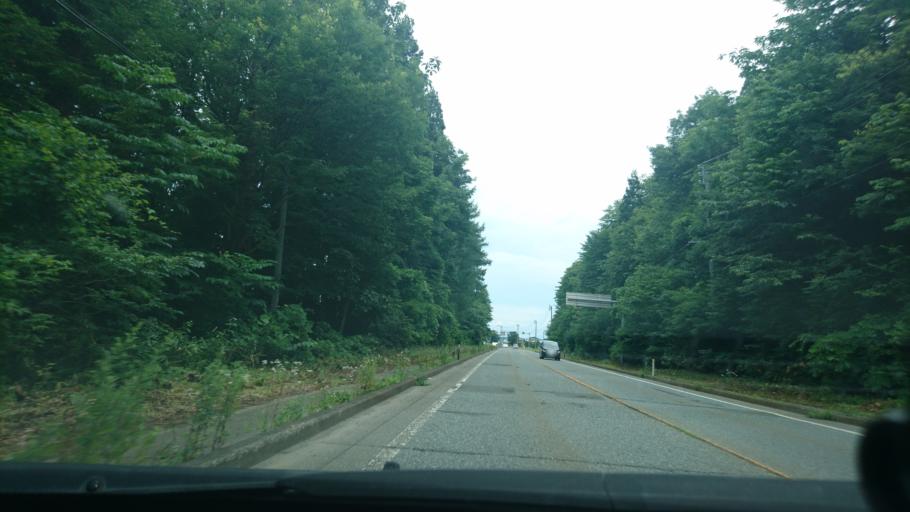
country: JP
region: Akita
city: Yokotemachi
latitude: 39.3879
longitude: 140.5678
